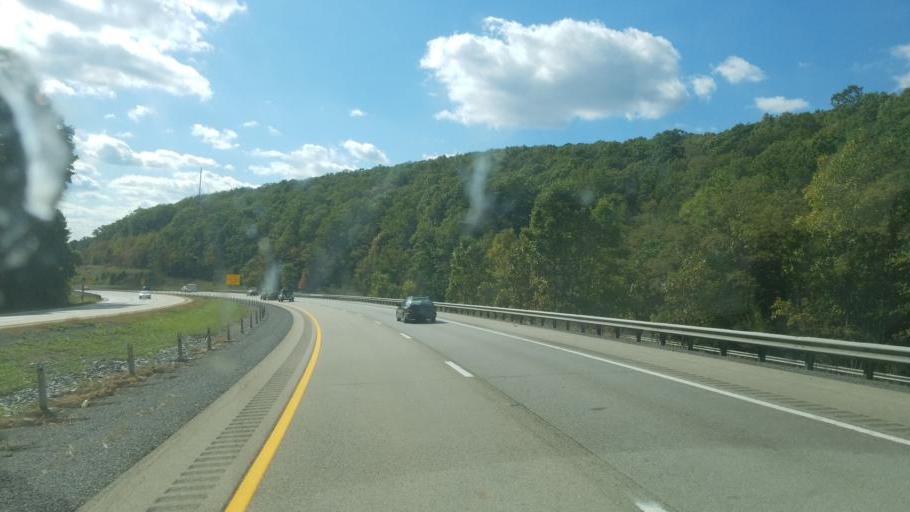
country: US
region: West Virginia
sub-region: Monongalia County
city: Cheat Lake
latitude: 39.6617
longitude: -79.8196
